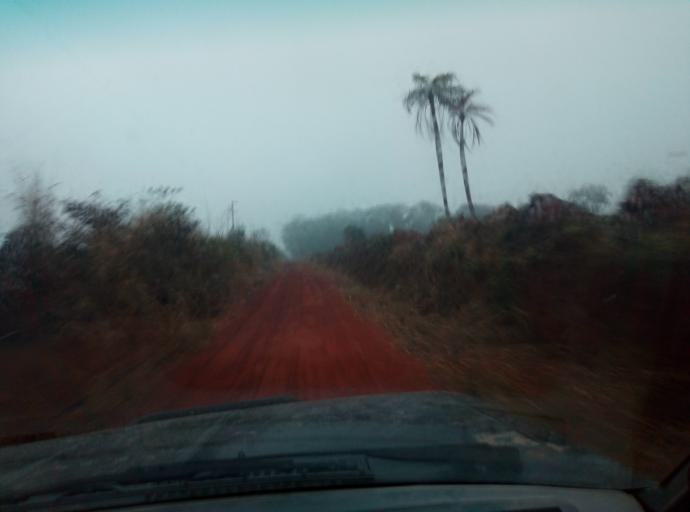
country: PY
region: Caaguazu
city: Doctor Cecilio Baez
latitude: -25.1586
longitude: -56.2660
